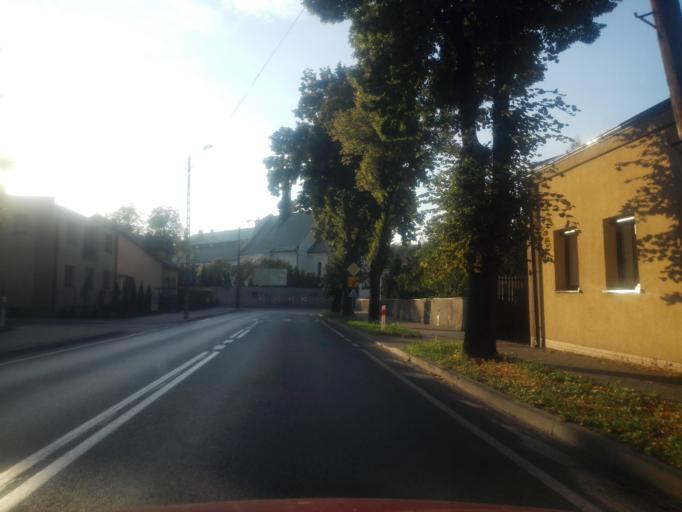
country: PL
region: Lodz Voivodeship
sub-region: Powiat wielunski
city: Wielun
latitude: 51.2166
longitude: 18.5742
